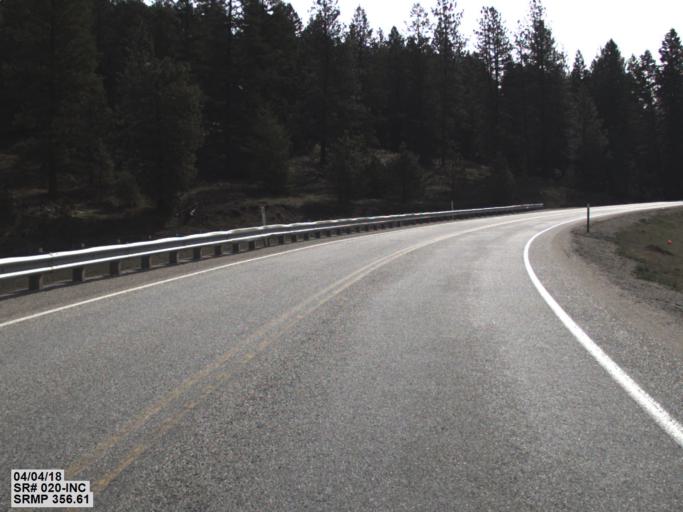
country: US
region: Washington
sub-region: Stevens County
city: Colville
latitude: 48.5471
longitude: -117.8568
